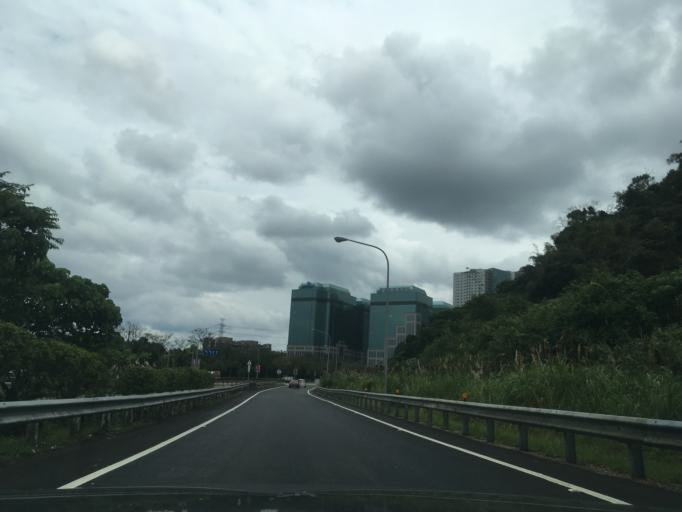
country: TW
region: Taipei
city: Taipei
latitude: 25.0569
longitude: 121.6419
